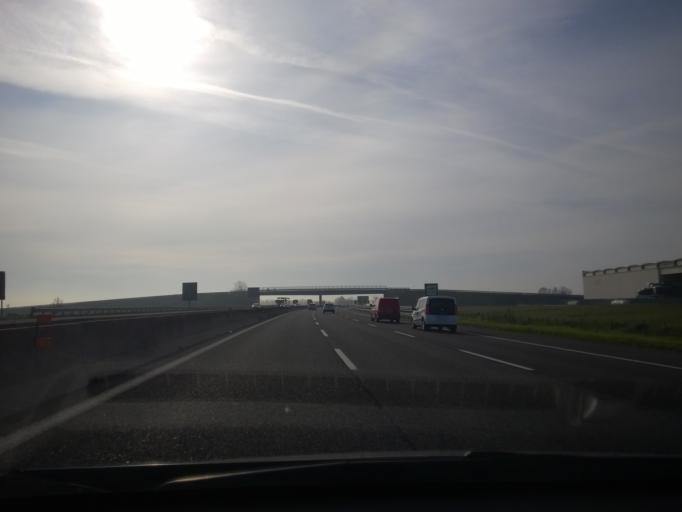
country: IT
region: Emilia-Romagna
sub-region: Provincia di Bologna
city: Castel San Pietro Terme
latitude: 44.4232
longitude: 11.6159
